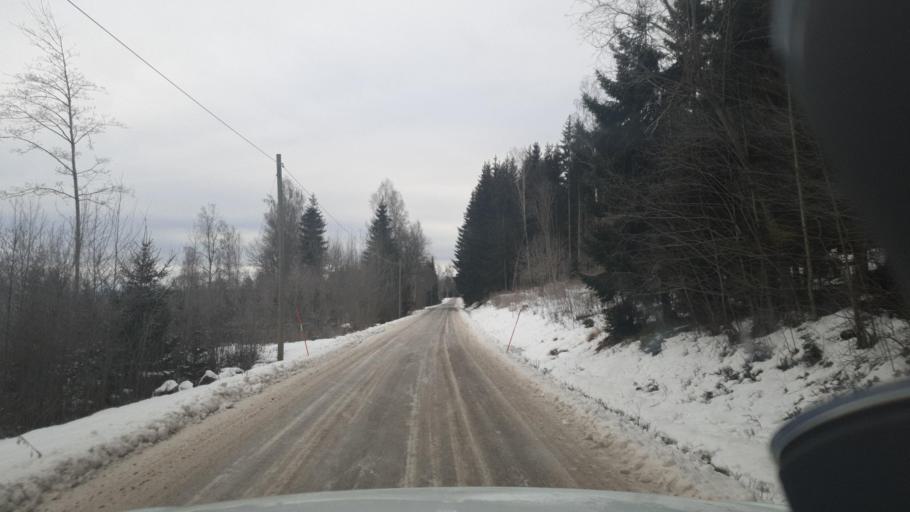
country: SE
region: Vaermland
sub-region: Eda Kommun
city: Amotfors
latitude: 59.7457
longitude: 12.2756
